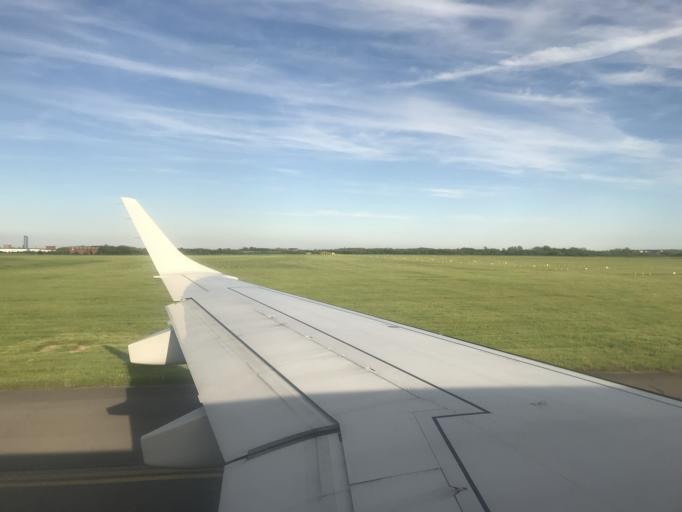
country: PL
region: Lower Silesian Voivodeship
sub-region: Powiat wroclawski
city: Smolec
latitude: 51.0999
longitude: 16.8984
